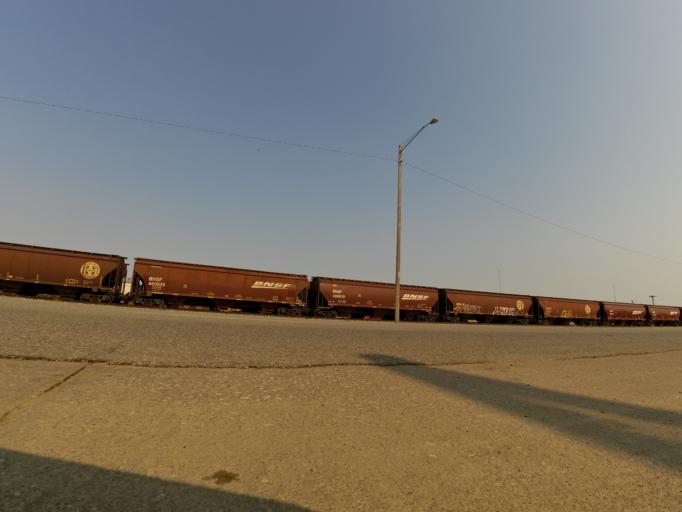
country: US
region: Kansas
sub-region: Sedgwick County
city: Wichita
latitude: 37.7343
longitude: -97.3361
